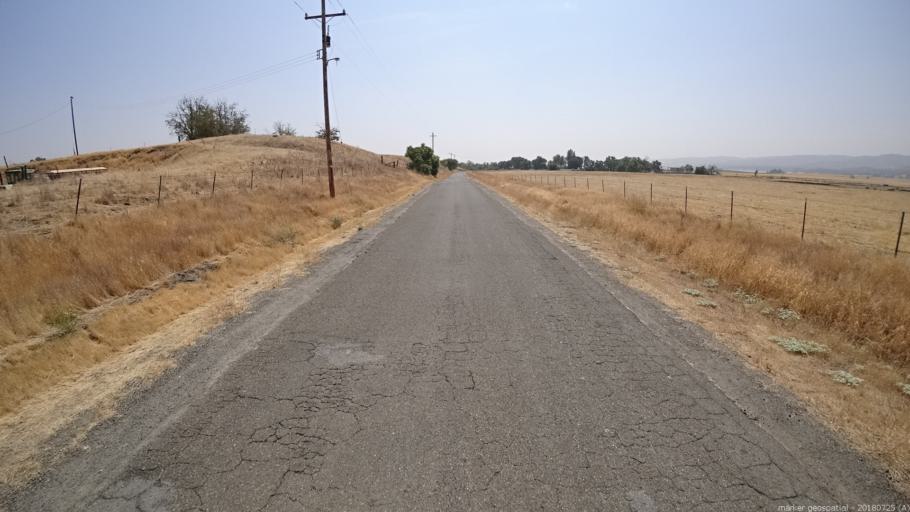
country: US
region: California
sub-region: San Luis Obispo County
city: Shandon
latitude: 35.8488
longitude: -120.3815
